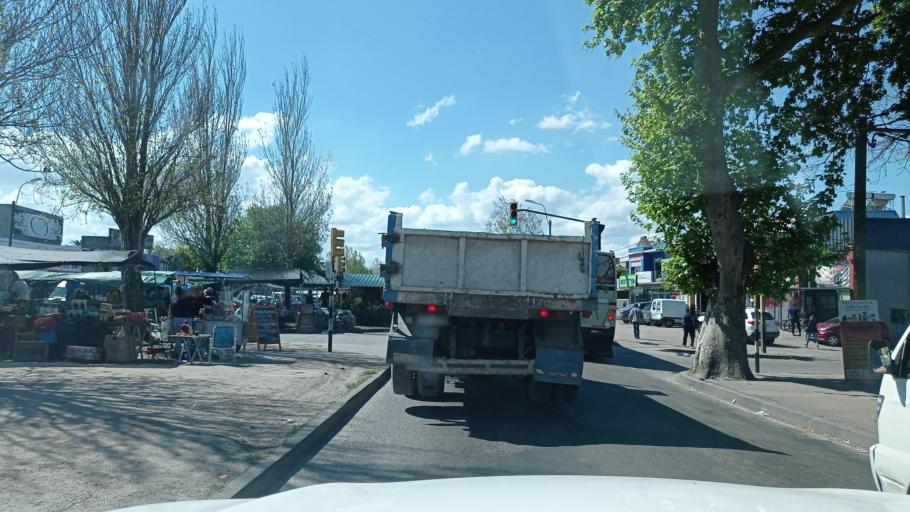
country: UY
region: Montevideo
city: Montevideo
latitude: -34.8274
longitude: -56.1408
